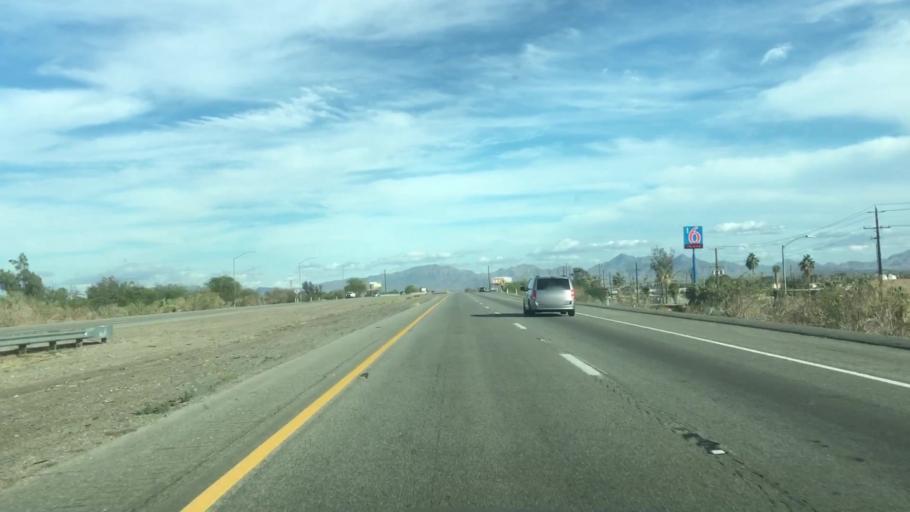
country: US
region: California
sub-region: Riverside County
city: Blythe
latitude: 33.6070
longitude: -114.6046
